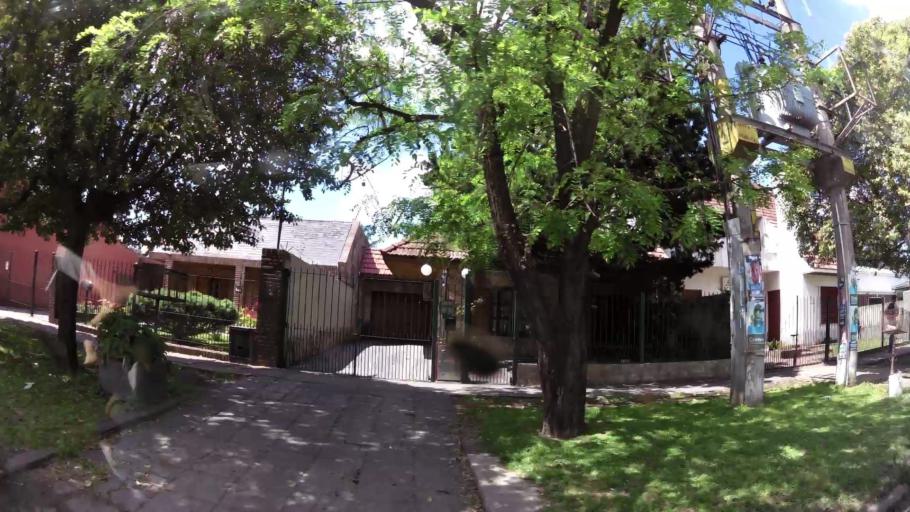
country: AR
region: Buenos Aires
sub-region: Partido de Quilmes
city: Quilmes
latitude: -34.8081
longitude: -58.2614
